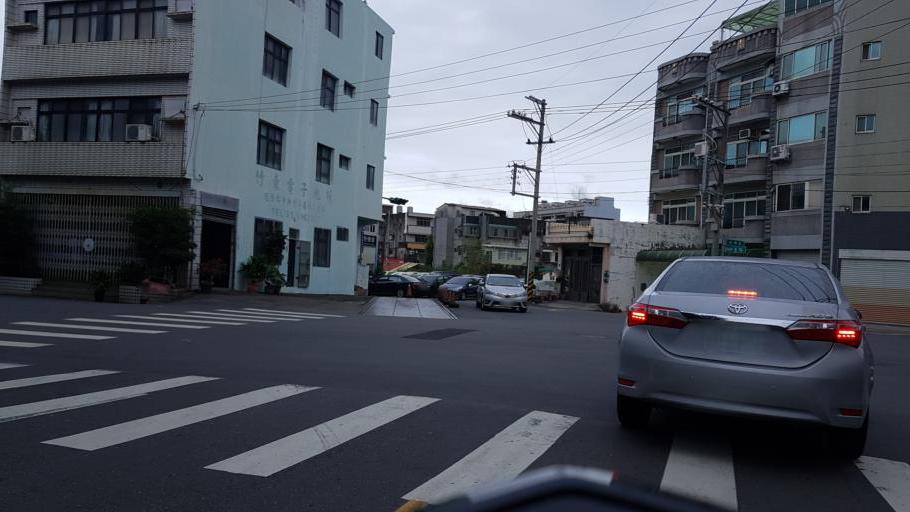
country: TW
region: Taiwan
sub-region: Hsinchu
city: Zhubei
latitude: 24.7355
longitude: 121.0953
